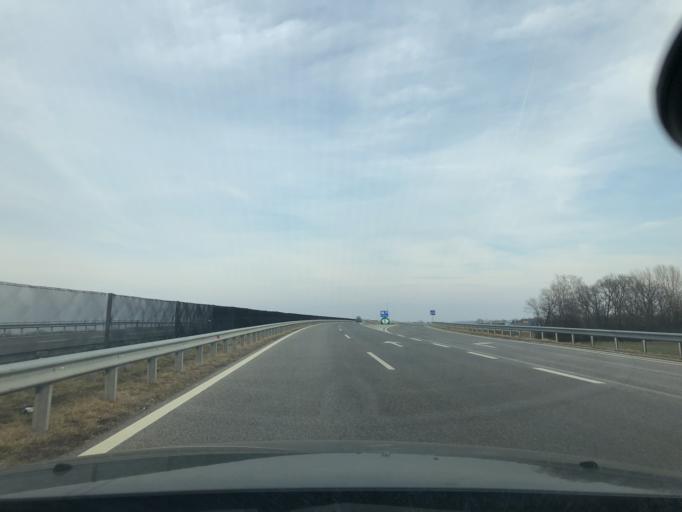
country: HU
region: Gyor-Moson-Sopron
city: Kony
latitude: 47.6380
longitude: 17.3445
